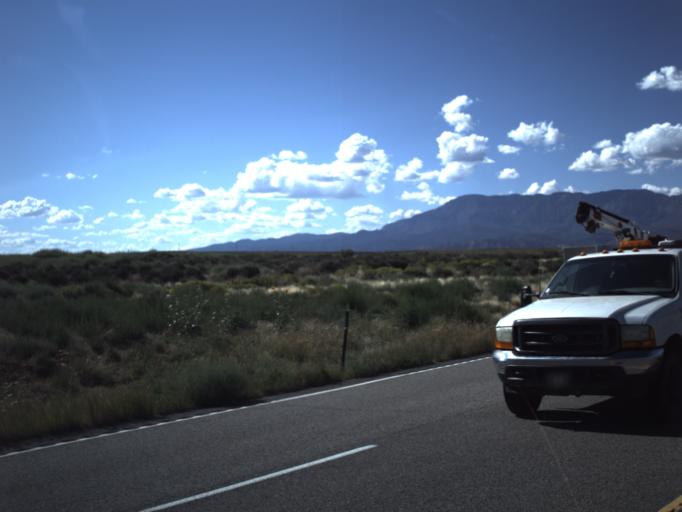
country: US
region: Utah
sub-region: Washington County
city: Hurricane
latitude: 37.1581
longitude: -113.2599
